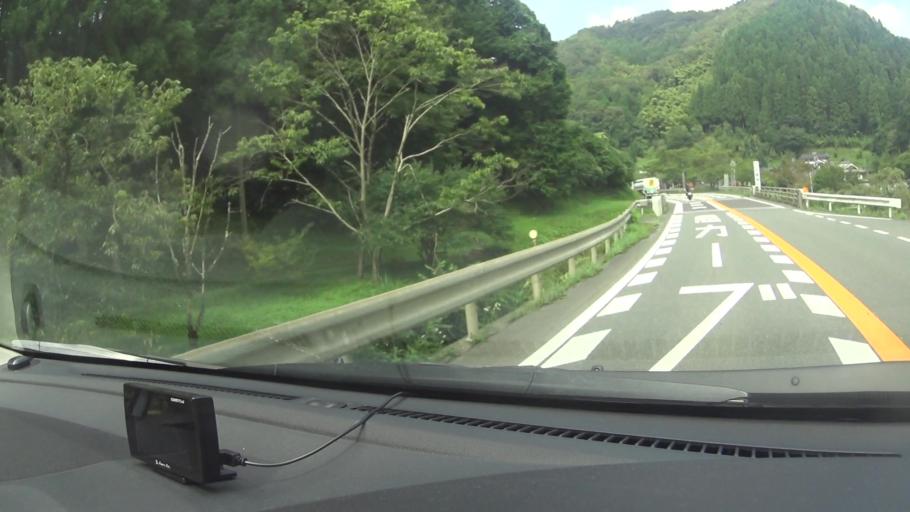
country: JP
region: Kyoto
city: Ayabe
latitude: 35.2443
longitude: 135.2944
